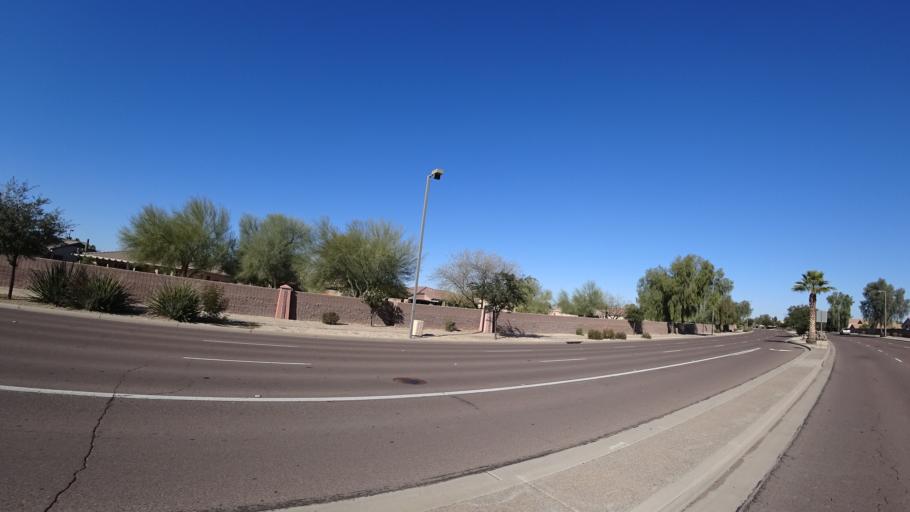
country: US
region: Arizona
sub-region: Maricopa County
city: Sun City West
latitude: 33.6491
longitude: -112.3823
